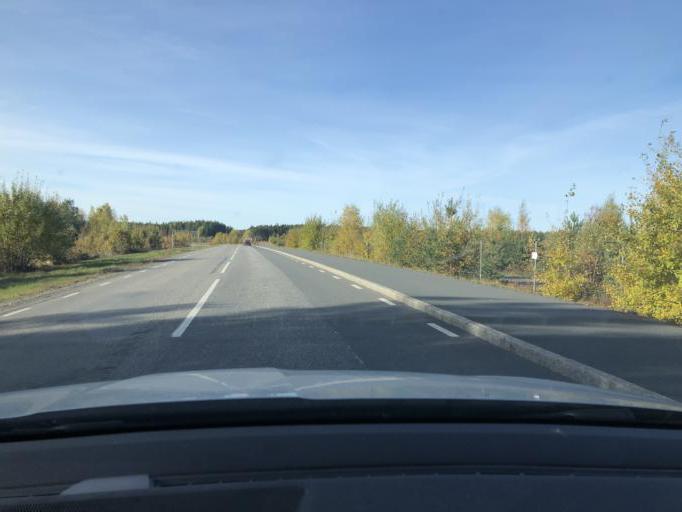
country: SE
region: Joenkoeping
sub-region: Jonkopings Kommun
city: Jonkoping
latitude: 57.7732
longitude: 14.0843
